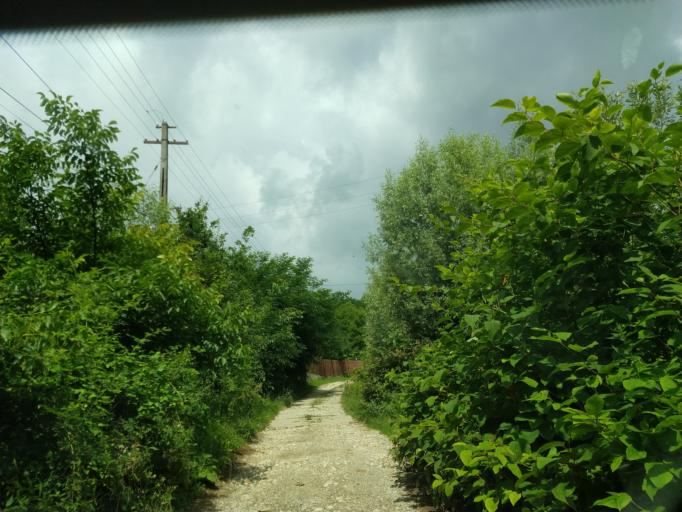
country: RO
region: Prahova
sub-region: Oras Breaza
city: Valea Tarsei
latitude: 45.1858
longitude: 25.6269
